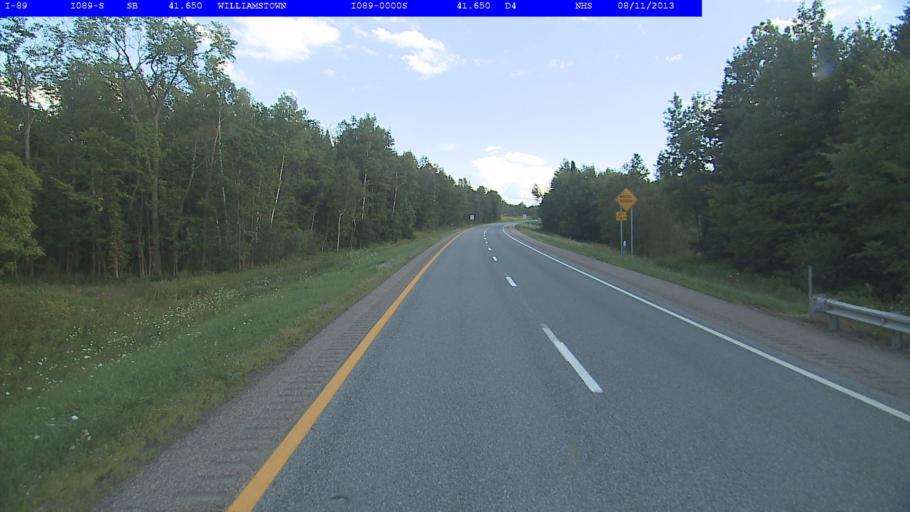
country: US
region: Vermont
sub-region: Washington County
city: Northfield
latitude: 44.0970
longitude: -72.6121
